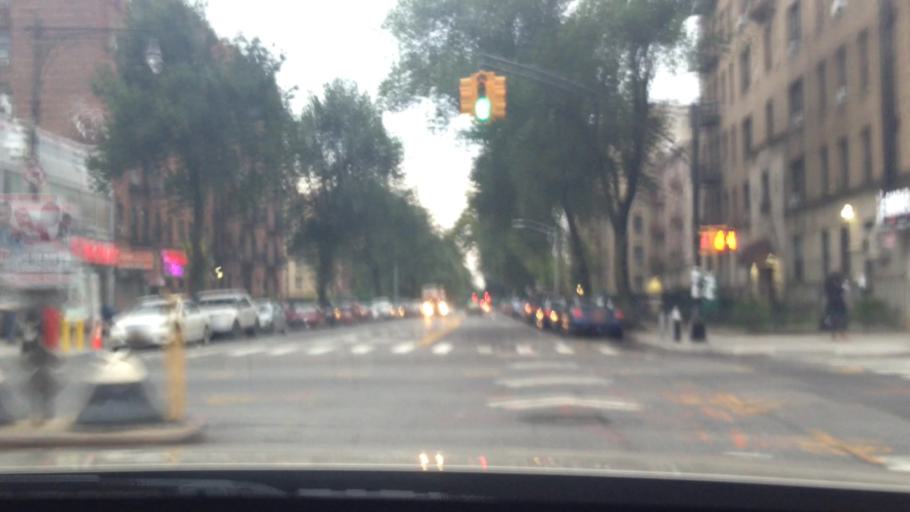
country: US
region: New York
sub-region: Kings County
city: Brooklyn
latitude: 40.6502
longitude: -73.9610
